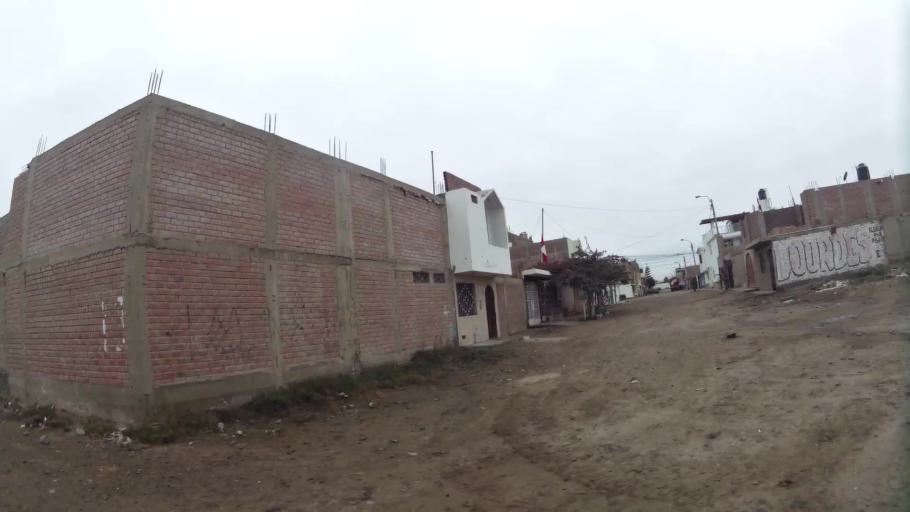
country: PE
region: Ica
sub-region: Provincia de Pisco
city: Pisco
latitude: -13.7172
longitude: -76.2162
